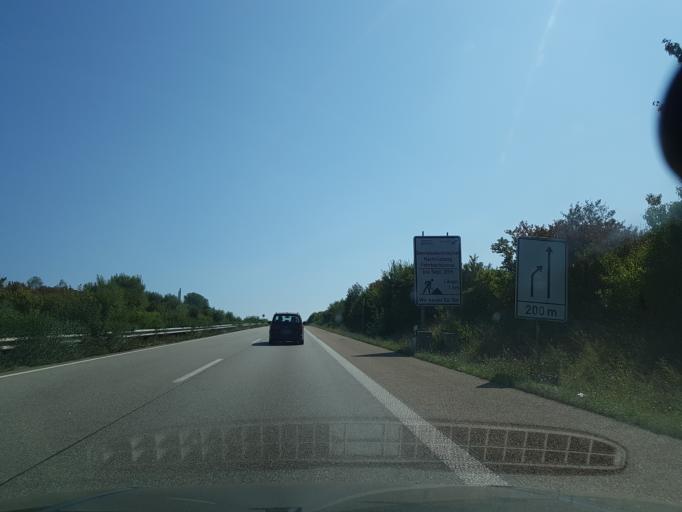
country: DE
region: Rheinland-Pfalz
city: Petersberg
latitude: 49.2327
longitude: 7.5697
